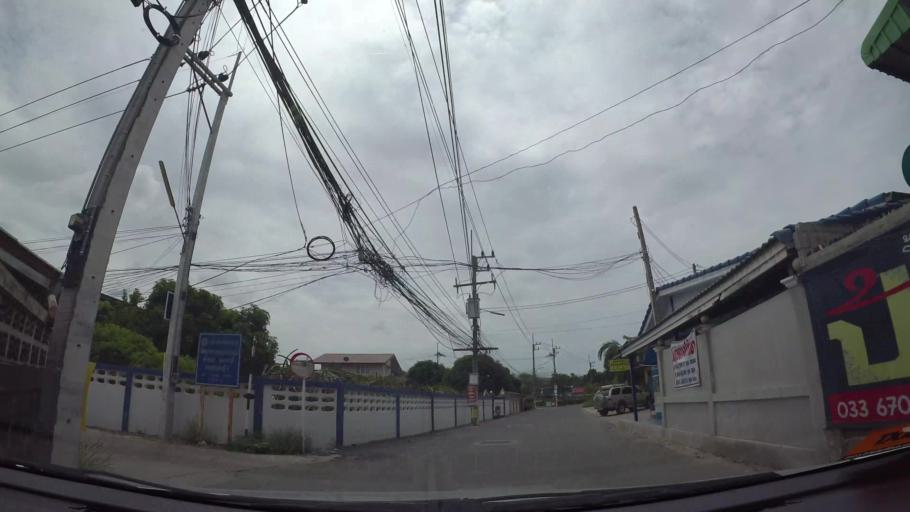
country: TH
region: Chon Buri
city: Sattahip
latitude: 12.6801
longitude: 100.8952
